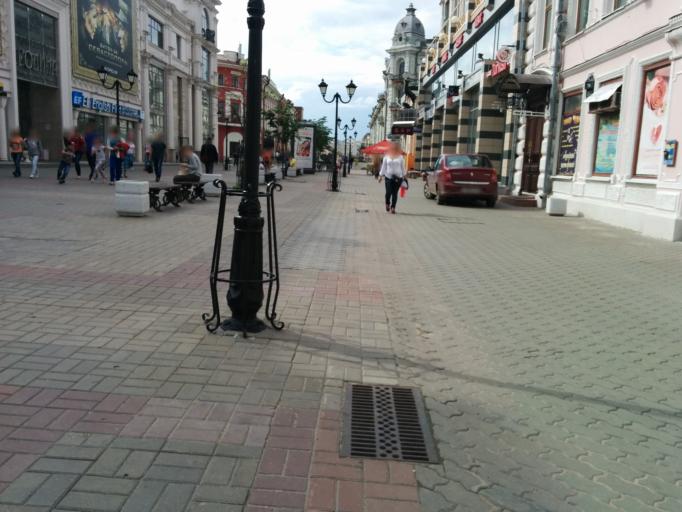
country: RU
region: Tatarstan
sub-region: Gorod Kazan'
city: Kazan
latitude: 55.7916
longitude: 49.1132
